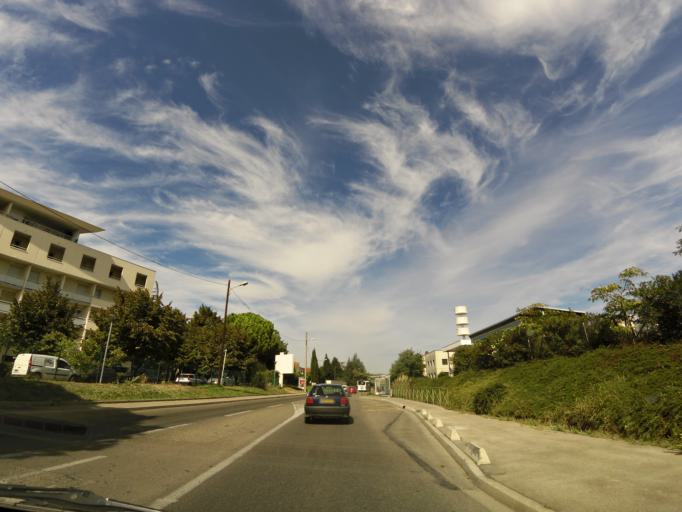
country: FR
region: Languedoc-Roussillon
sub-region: Departement du Gard
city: Nimes
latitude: 43.8185
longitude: 4.3661
